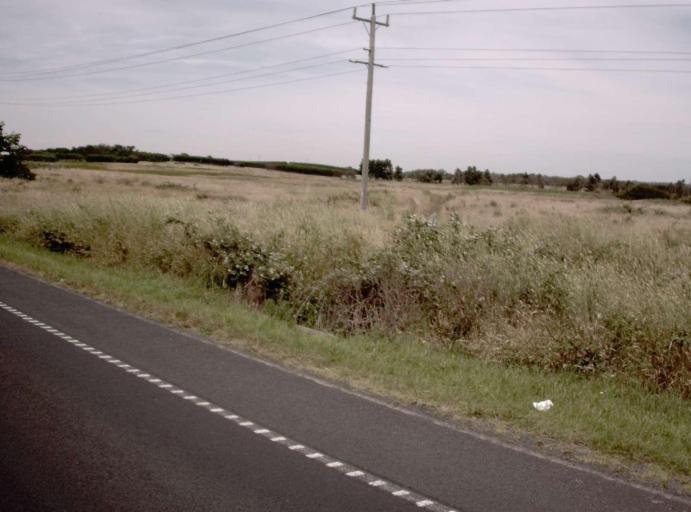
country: AU
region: Victoria
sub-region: Mornington Peninsula
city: Tyabb
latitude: -38.2324
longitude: 145.2161
